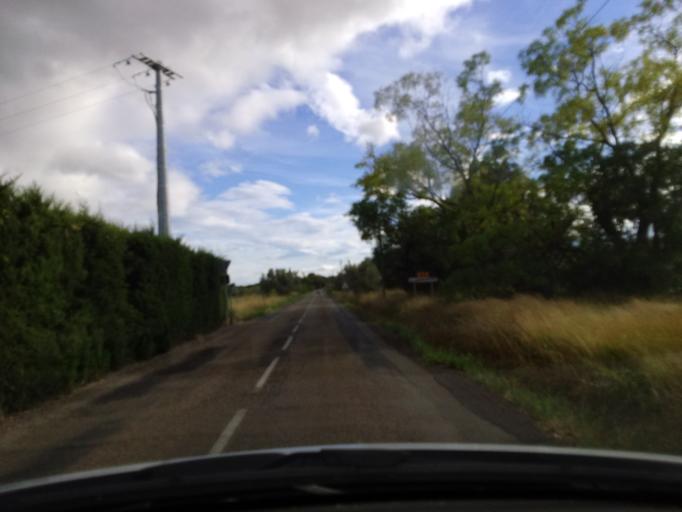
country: FR
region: Languedoc-Roussillon
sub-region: Departement de l'Herault
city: Saint-Jean-de-Fos
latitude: 43.6950
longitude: 3.5463
